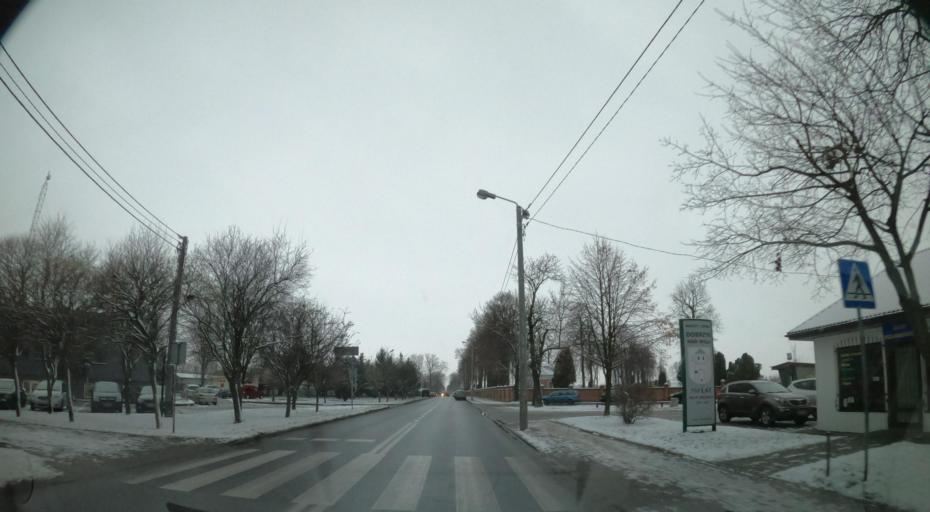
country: PL
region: Kujawsko-Pomorskie
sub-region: Powiat lipnowski
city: Dobrzyn nad Wisla
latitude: 52.6395
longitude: 19.3190
